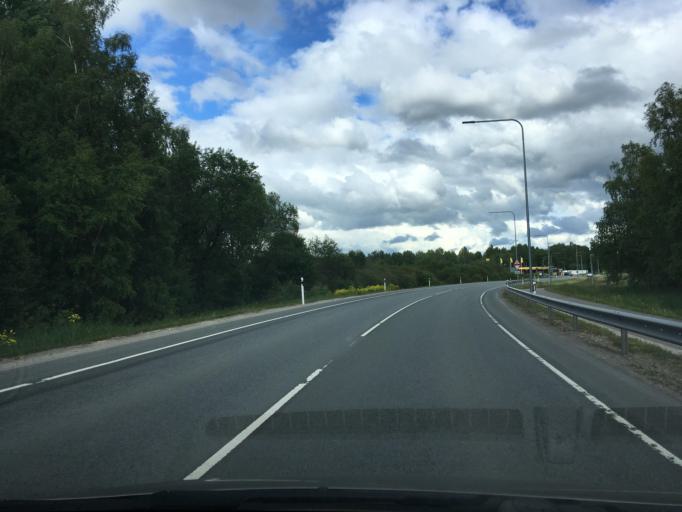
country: EE
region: Jaervamaa
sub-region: Paide linn
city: Paide
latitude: 58.8945
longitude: 25.5644
